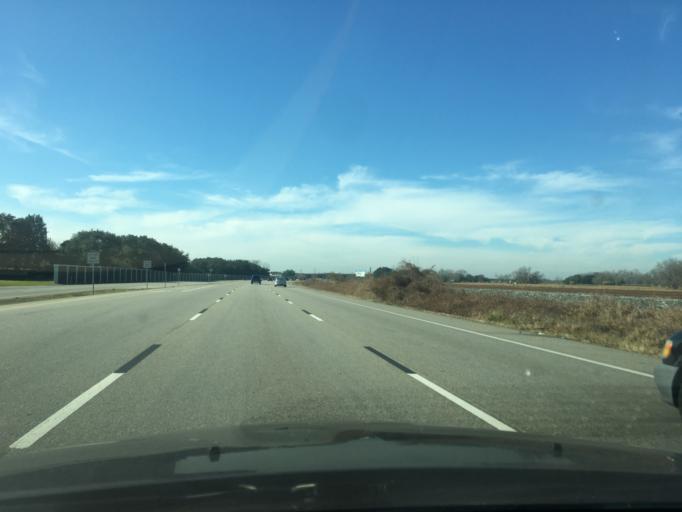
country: US
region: Texas
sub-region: Fort Bend County
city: New Territory
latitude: 29.6039
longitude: -95.6732
